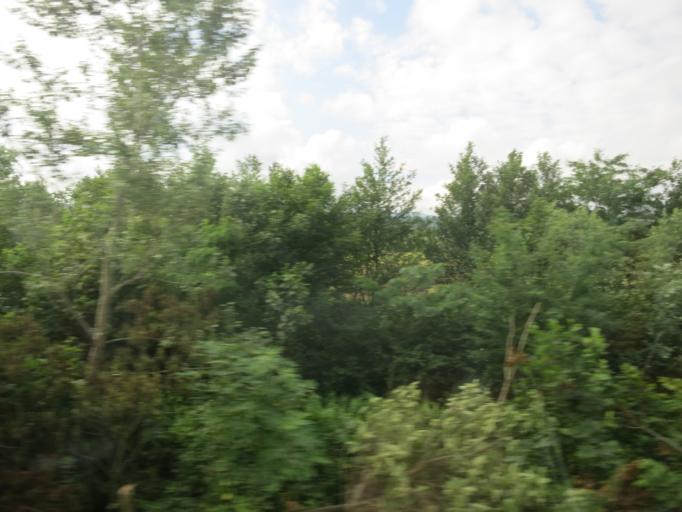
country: GE
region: Guria
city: Lanchkhuti
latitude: 42.0836
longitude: 41.9423
